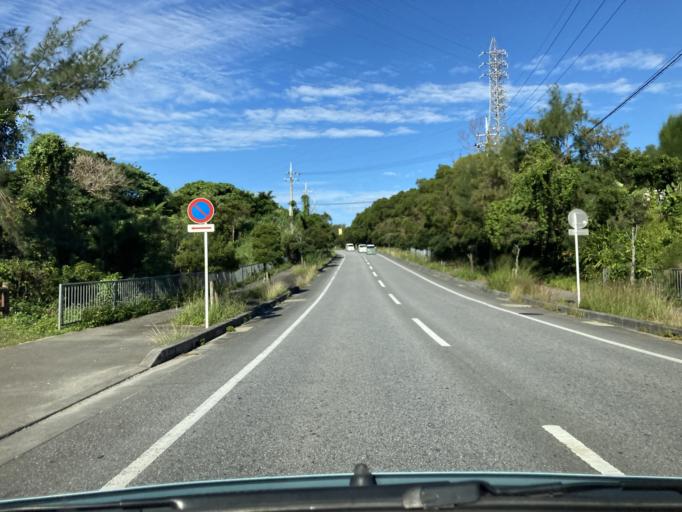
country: JP
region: Okinawa
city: Okinawa
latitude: 26.3712
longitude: 127.7690
